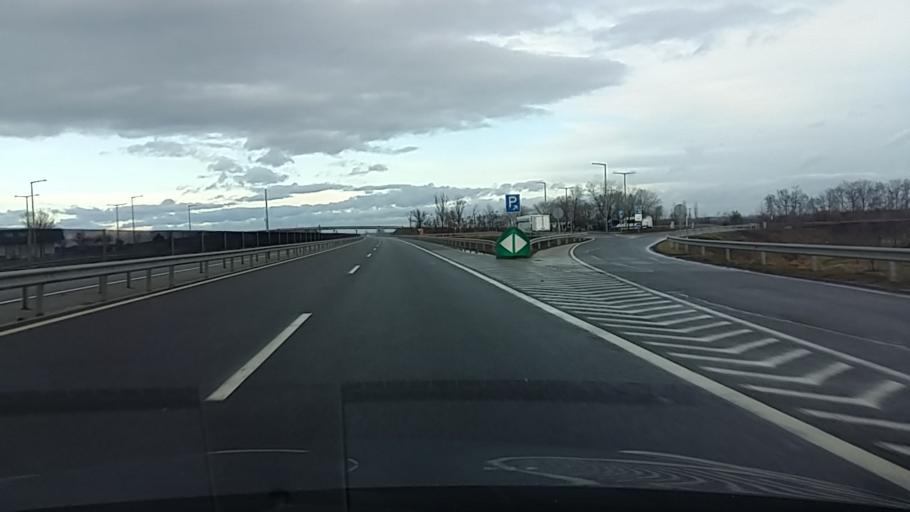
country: HU
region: Hajdu-Bihar
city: Gorbehaza
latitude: 47.8243
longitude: 21.3241
